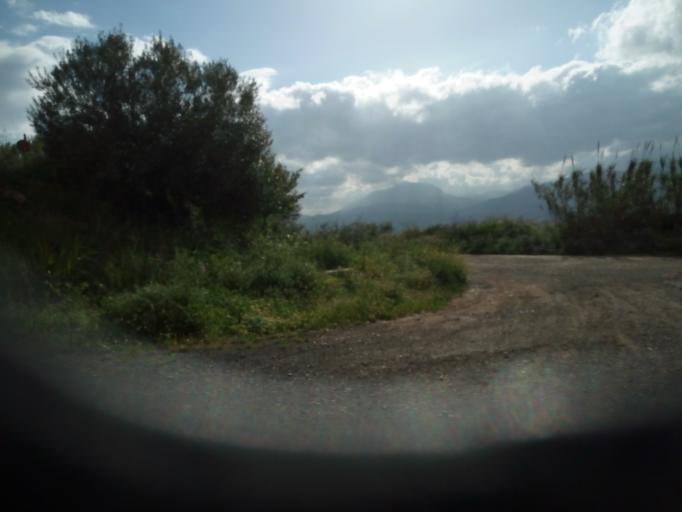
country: DZ
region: Tipaza
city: El Affroun
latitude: 36.3716
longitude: 2.5025
